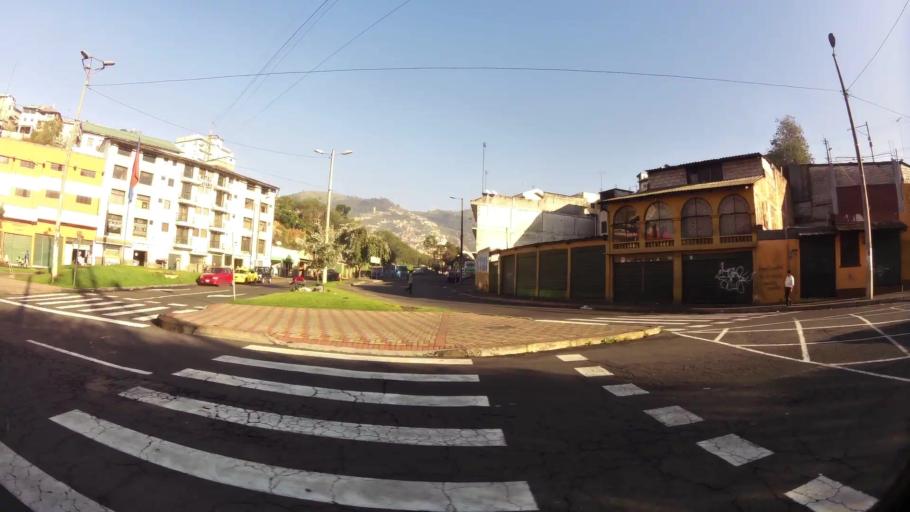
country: EC
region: Pichincha
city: Quito
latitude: -0.2273
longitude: -78.5071
